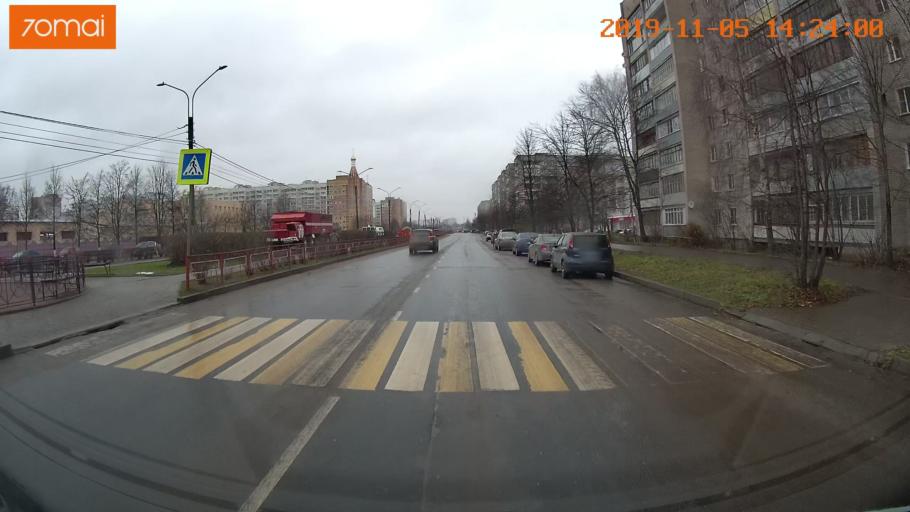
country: RU
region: Ivanovo
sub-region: Gorod Ivanovo
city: Ivanovo
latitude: 56.9663
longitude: 41.0005
